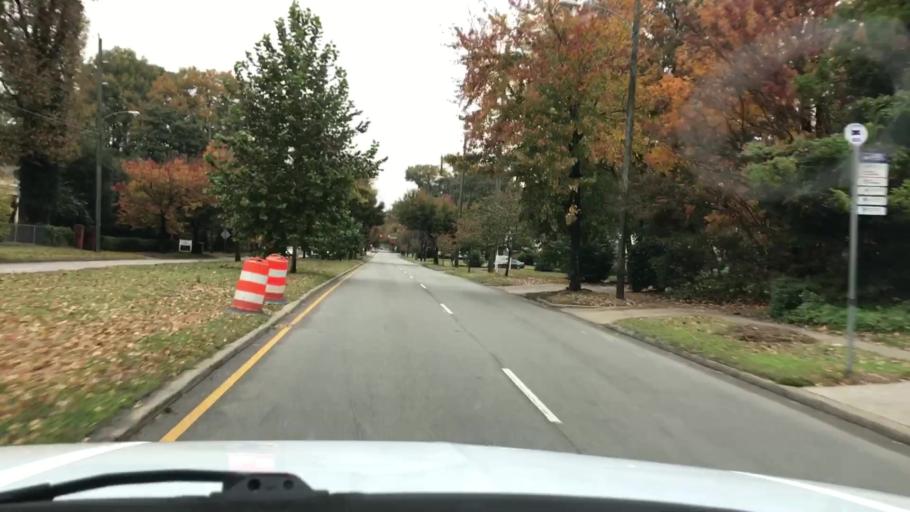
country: US
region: Virginia
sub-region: City of Richmond
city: Richmond
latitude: 37.5818
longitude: -77.4468
